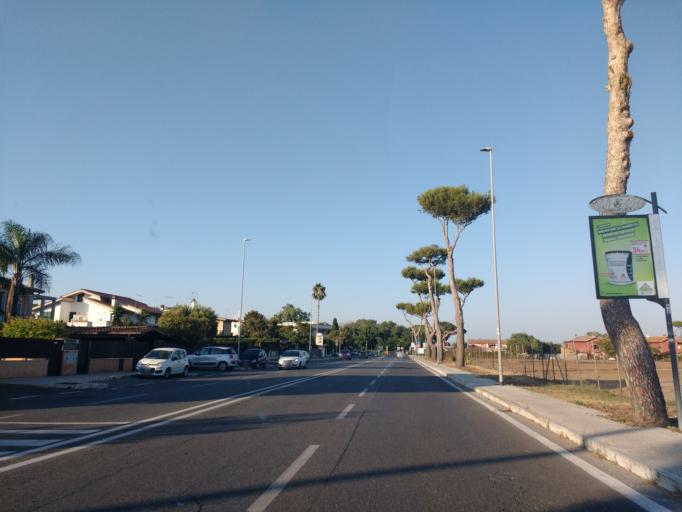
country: IT
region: Latium
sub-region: Citta metropolitana di Roma Capitale
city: Fregene
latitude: 41.8613
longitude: 12.2084
